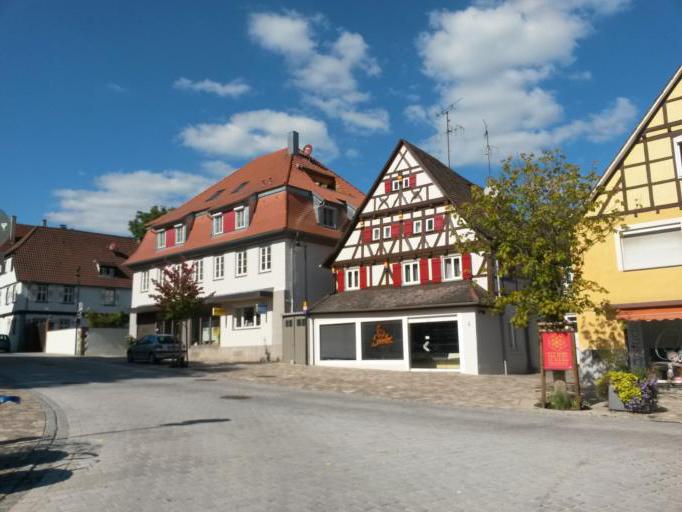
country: DE
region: Baden-Wuerttemberg
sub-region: Karlsruhe Region
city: Muhlacker
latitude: 48.9400
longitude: 8.8400
